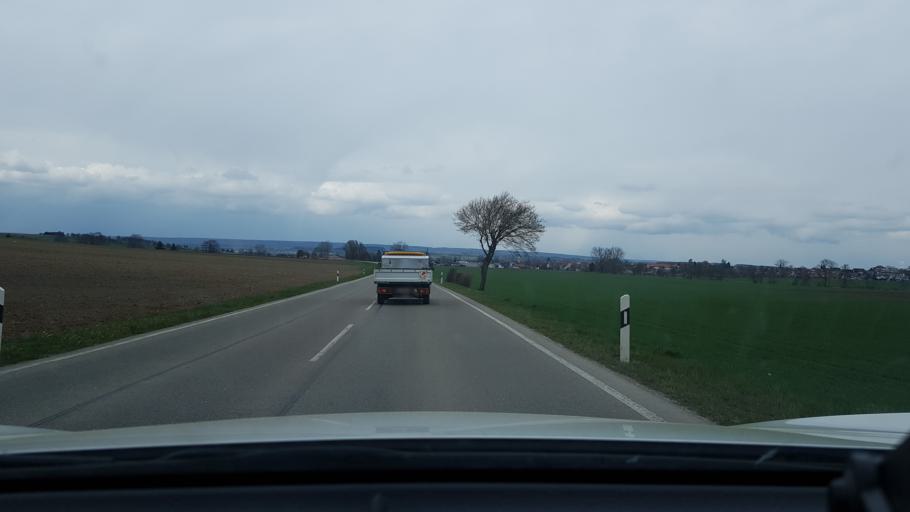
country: DE
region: Baden-Wuerttemberg
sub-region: Tuebingen Region
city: Oberstadion
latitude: 48.1908
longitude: 9.6906
